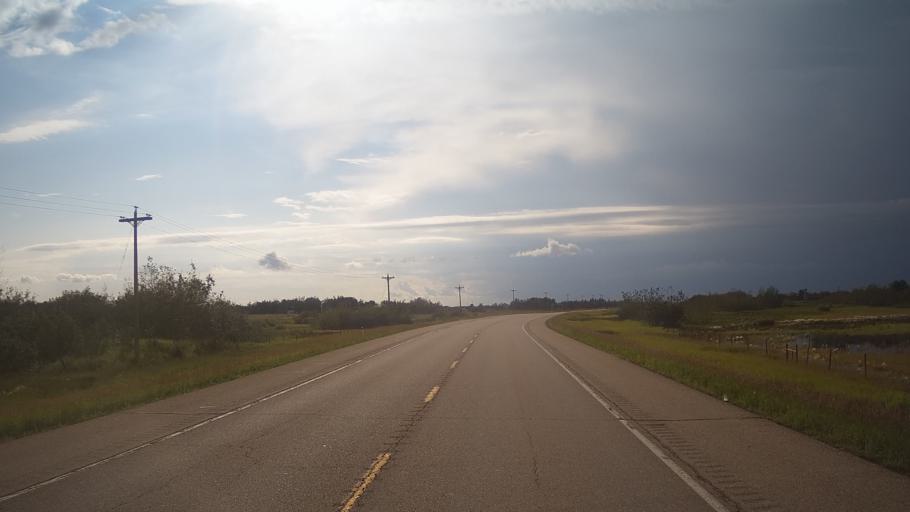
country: CA
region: Alberta
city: Viking
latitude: 53.1640
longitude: -112.0168
